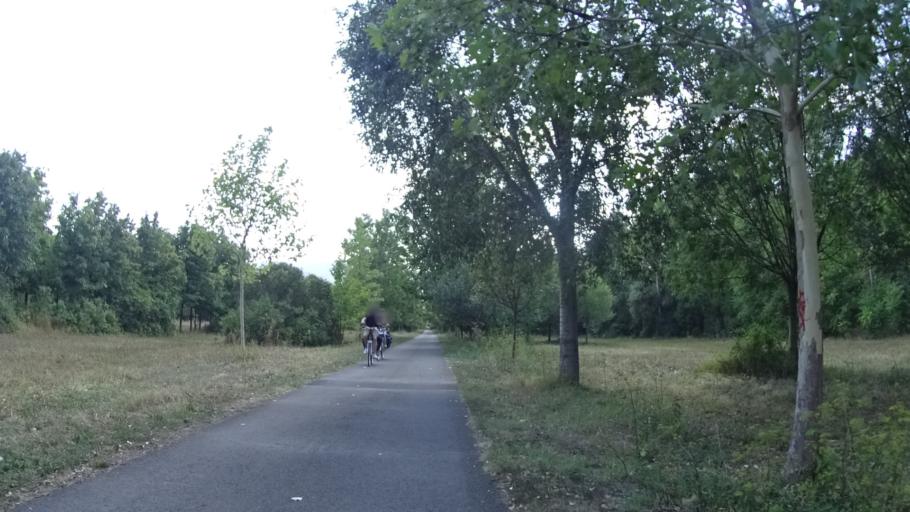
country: HU
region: Pest
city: Nagymaros
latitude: 47.7751
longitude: 18.9492
